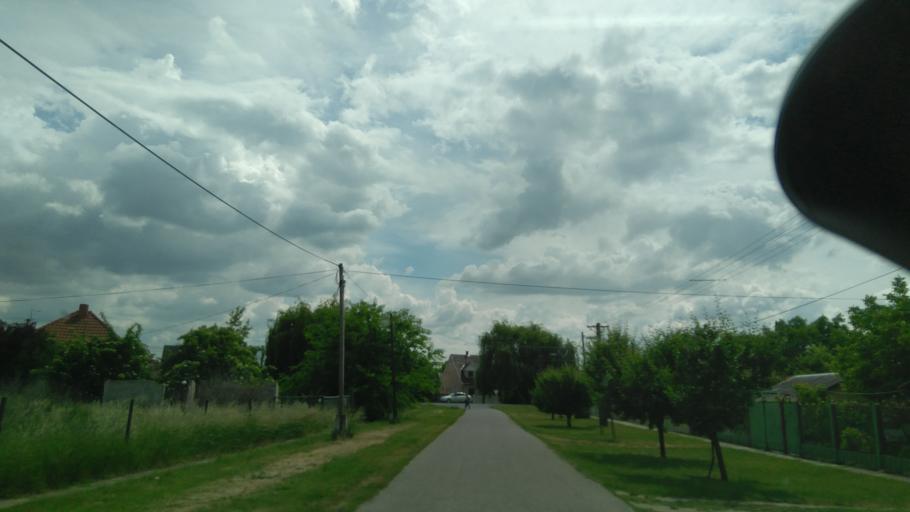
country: HU
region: Bekes
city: Mezohegyes
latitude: 46.3208
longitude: 20.8101
